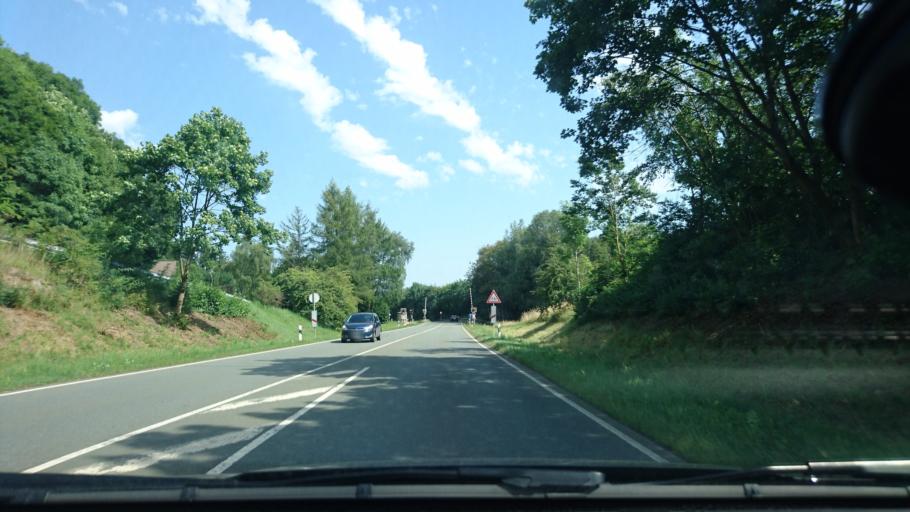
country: DE
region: Bavaria
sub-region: Upper Franconia
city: Selbitz
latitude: 50.3169
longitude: 11.7389
